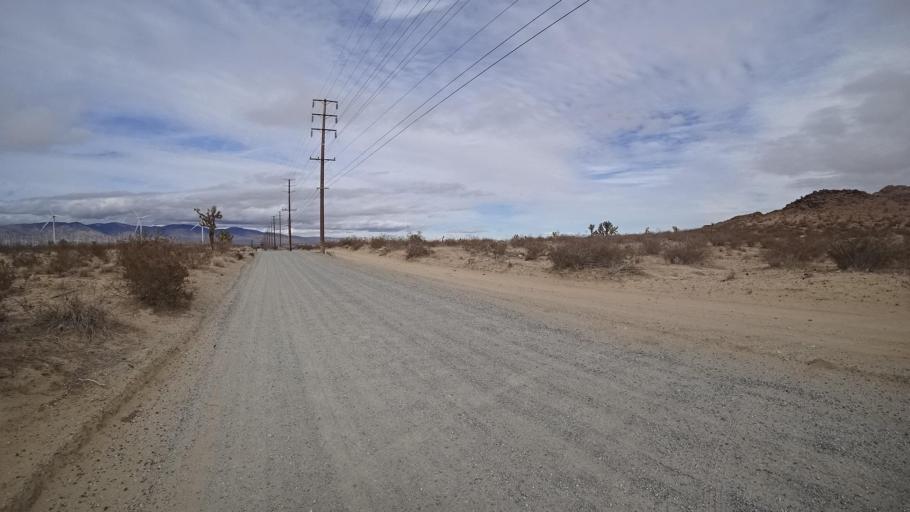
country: US
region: California
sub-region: Kern County
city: Mojave
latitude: 35.0079
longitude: -118.1858
